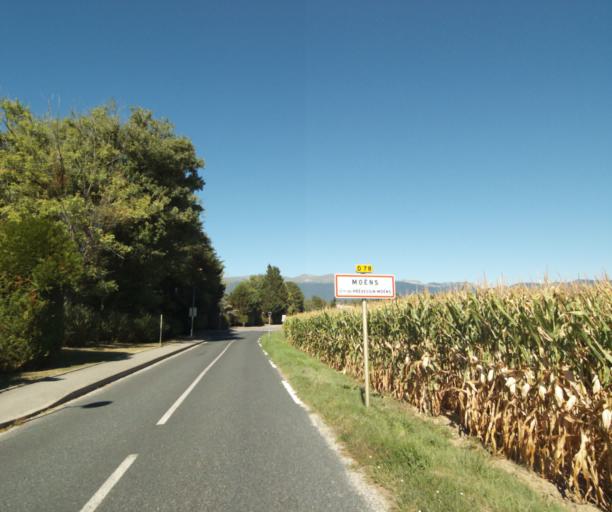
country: FR
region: Rhone-Alpes
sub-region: Departement de l'Ain
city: Ferney-Voltaire
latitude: 46.2596
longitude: 6.1001
